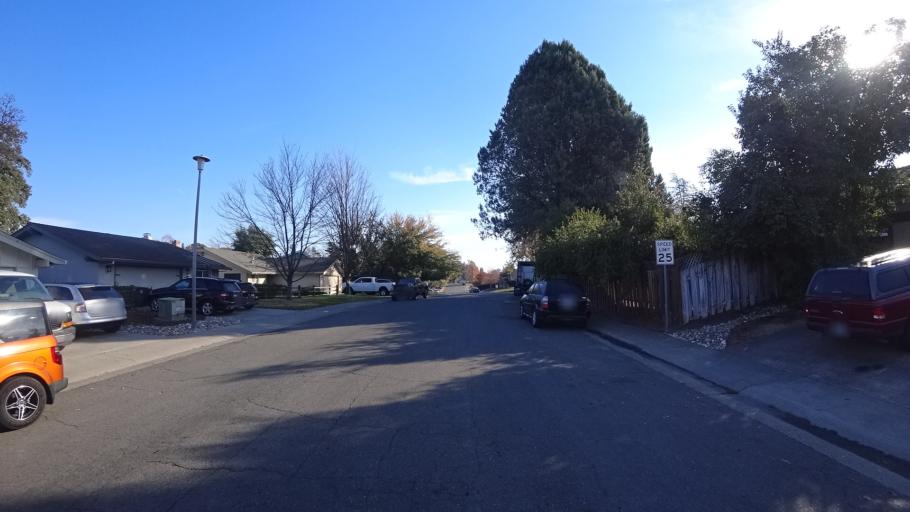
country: US
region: California
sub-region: Sacramento County
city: Antelope
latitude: 38.6803
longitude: -121.3099
